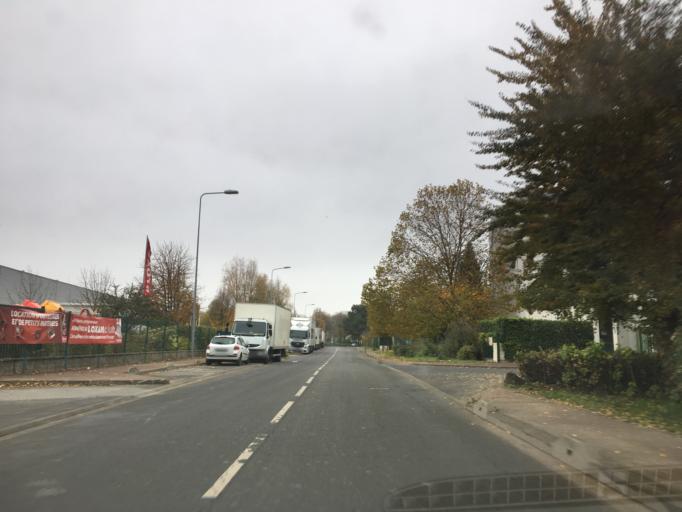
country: FR
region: Ile-de-France
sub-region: Departement du Val-de-Marne
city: Saint-Maur-des-Fosses
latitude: 48.7811
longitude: 2.5051
